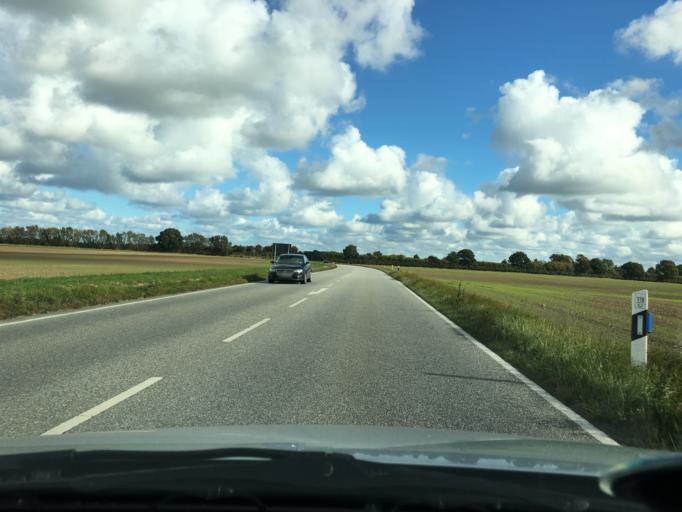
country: DE
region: Schleswig-Holstein
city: Prasdorf
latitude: 54.3962
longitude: 10.2965
